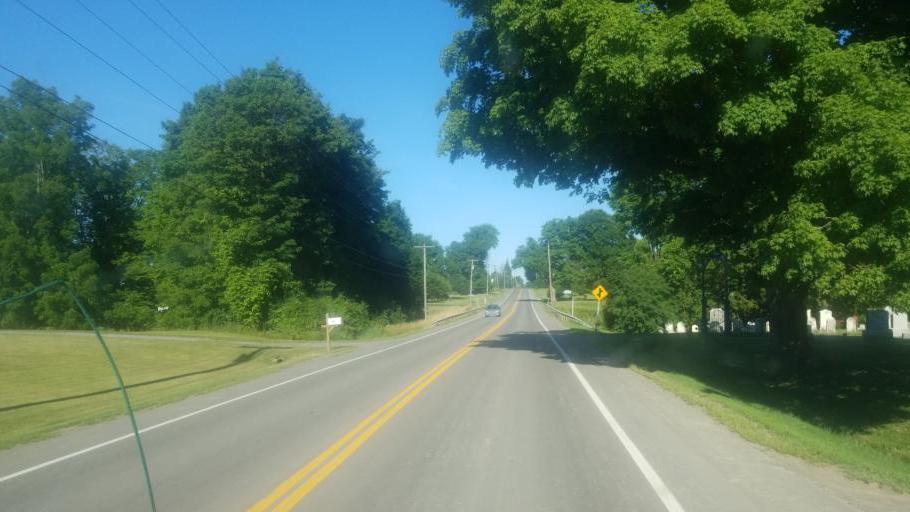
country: US
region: New York
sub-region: Ontario County
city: Phelps
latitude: 42.8862
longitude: -77.0741
